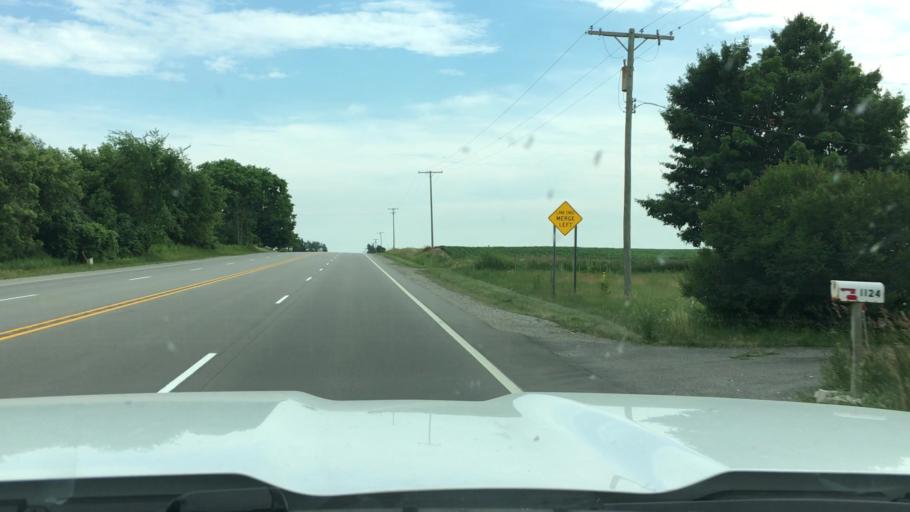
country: US
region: Michigan
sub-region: Sanilac County
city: Marlette
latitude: 43.3825
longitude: -83.0860
